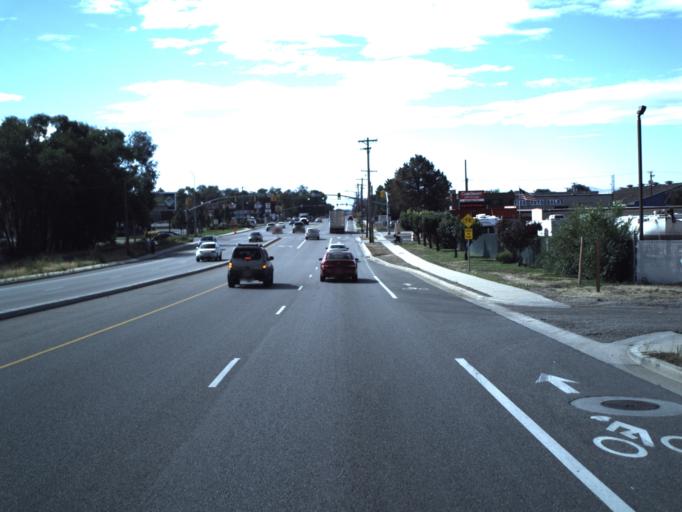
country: US
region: Utah
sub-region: Salt Lake County
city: Salt Lake City
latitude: 40.7621
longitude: -111.9392
